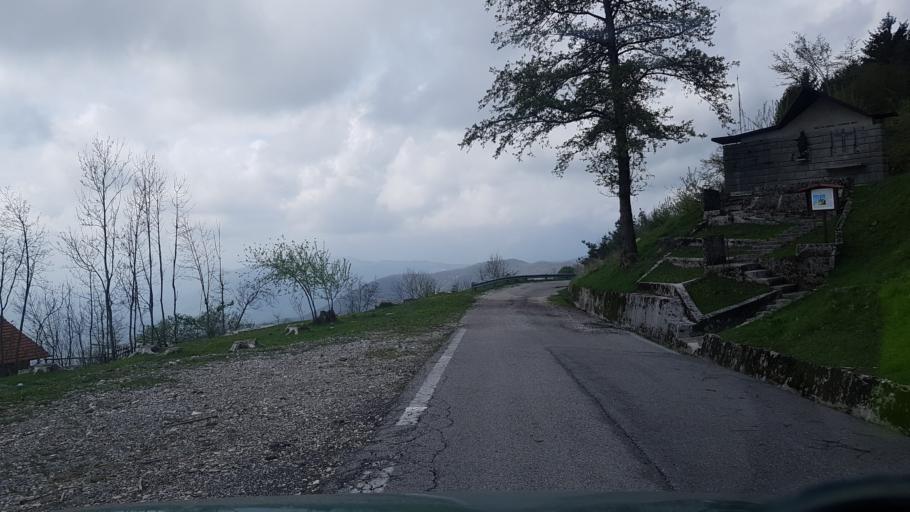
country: IT
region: Friuli Venezia Giulia
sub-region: Provincia di Udine
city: Faedis
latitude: 46.1877
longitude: 13.3634
